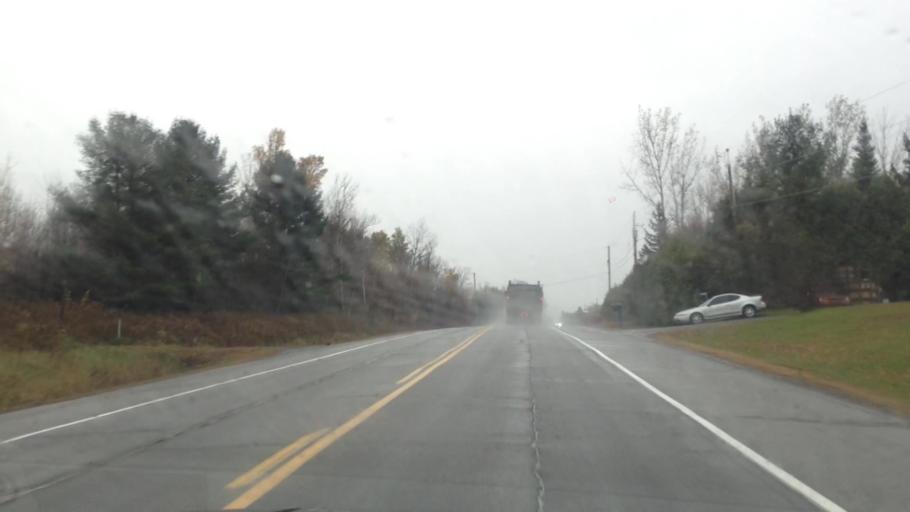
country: CA
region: Ontario
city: Clarence-Rockland
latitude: 45.3788
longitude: -75.3835
